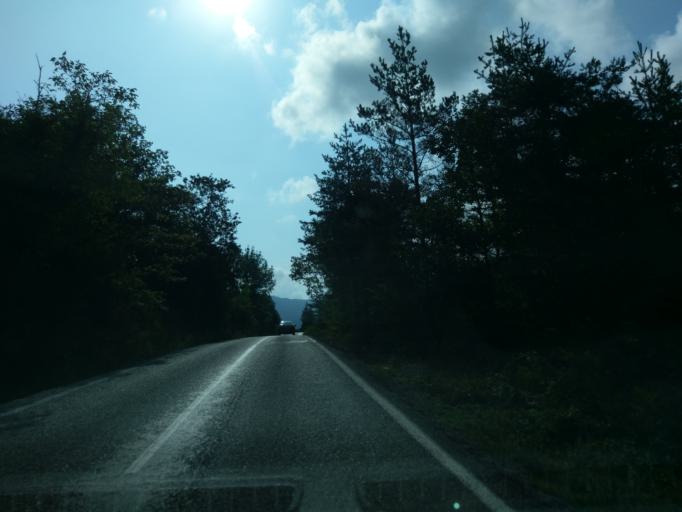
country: TR
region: Sinop
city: Ayancik
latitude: 41.8808
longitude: 34.5250
